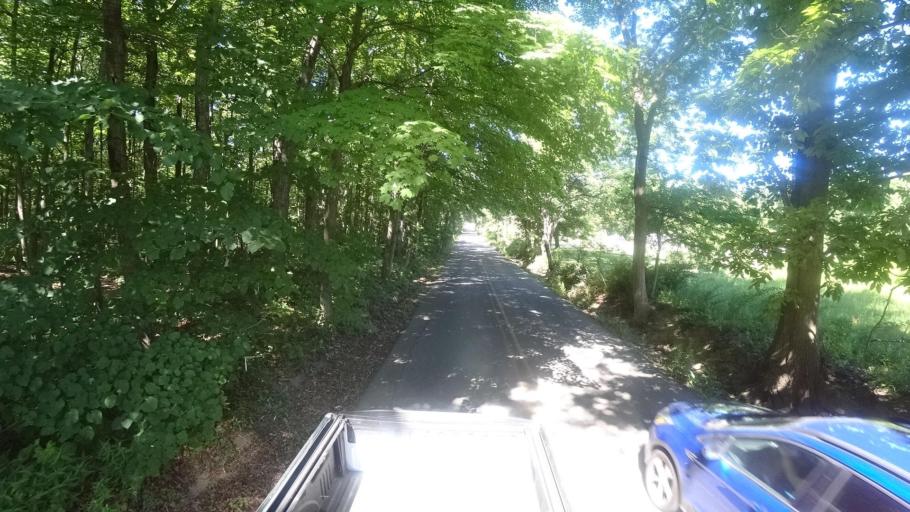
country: US
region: Indiana
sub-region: Porter County
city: Porter
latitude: 41.6297
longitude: -87.0834
